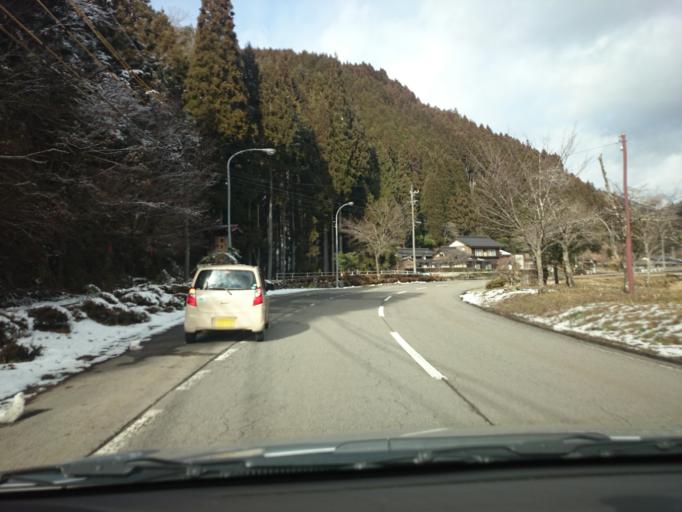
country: JP
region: Gifu
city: Gujo
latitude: 35.7436
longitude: 137.0506
